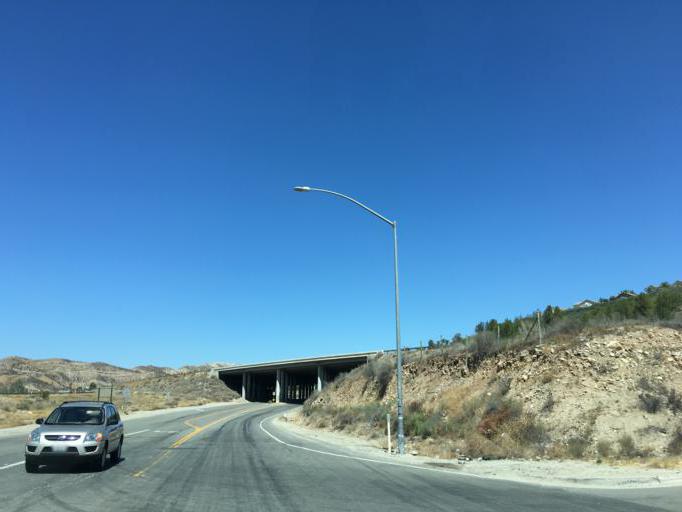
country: US
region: California
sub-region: Los Angeles County
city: Agua Dulce
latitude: 34.4327
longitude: -118.3840
